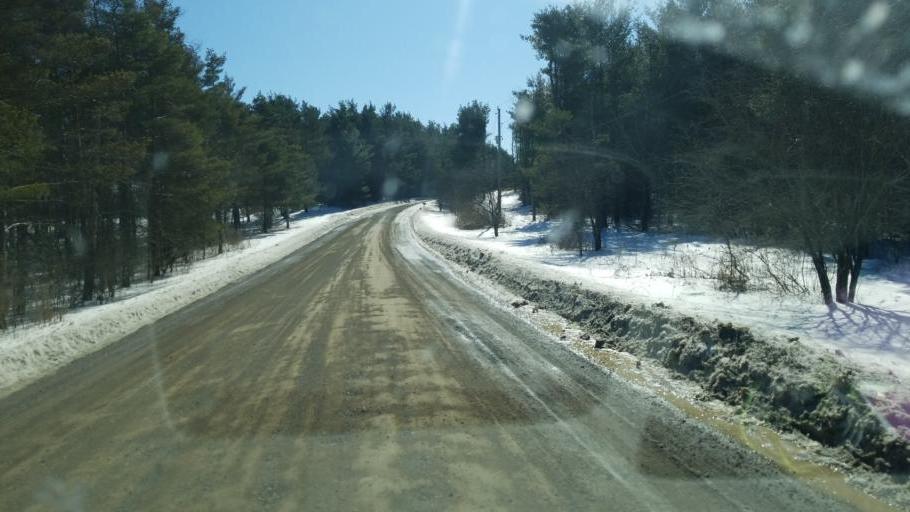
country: US
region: New York
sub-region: Allegany County
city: Alfred
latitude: 42.2565
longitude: -77.7320
